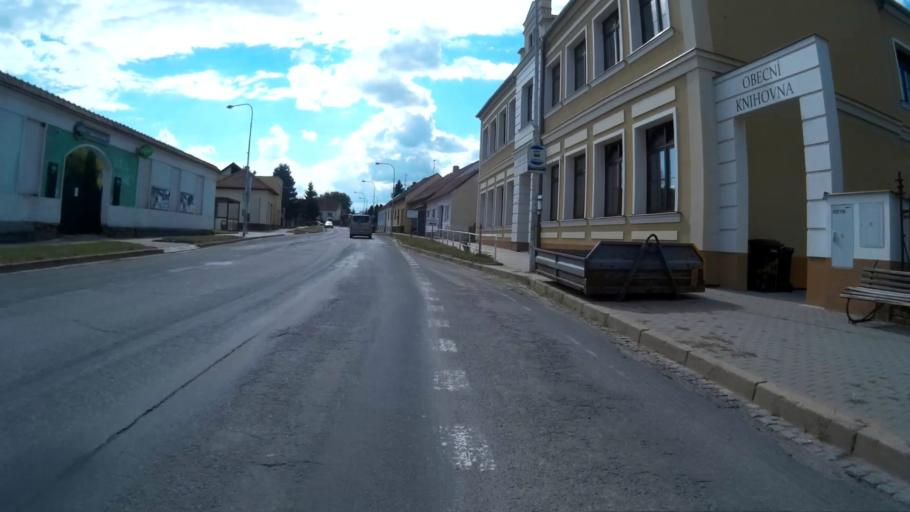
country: CZ
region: South Moravian
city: Strelice
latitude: 49.1527
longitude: 16.5033
